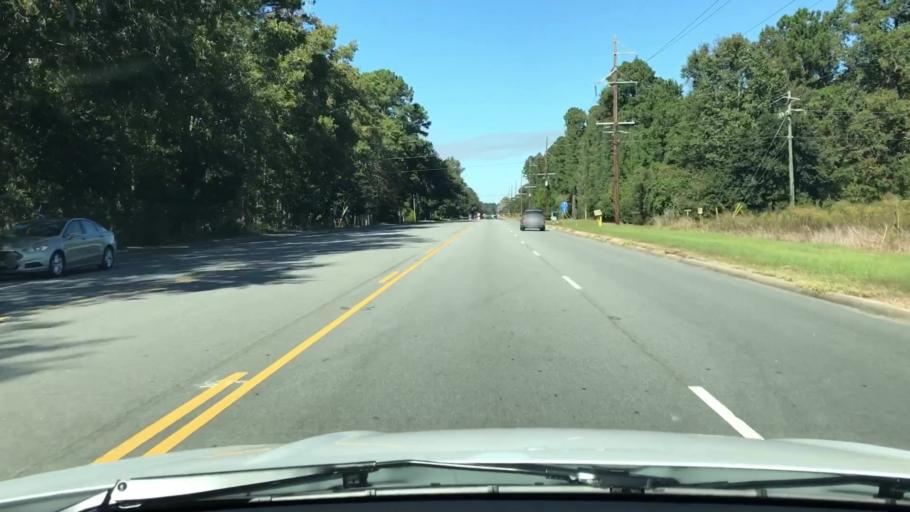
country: US
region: South Carolina
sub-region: Beaufort County
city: Laurel Bay
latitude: 32.5670
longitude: -80.7435
